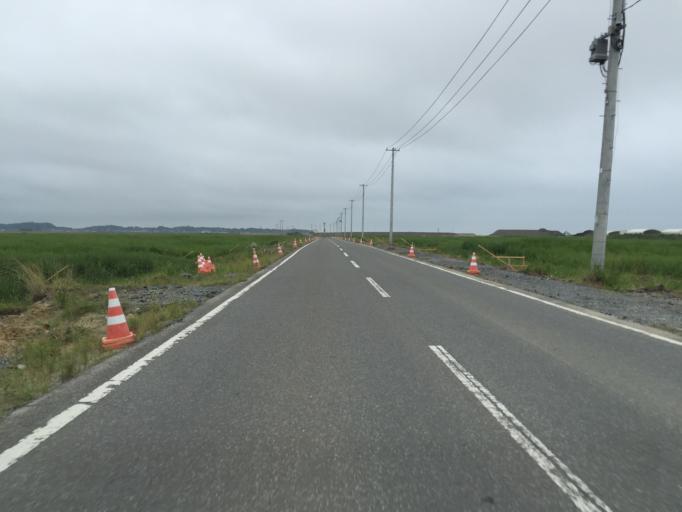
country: JP
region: Fukushima
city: Namie
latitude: 37.6798
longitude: 141.0038
